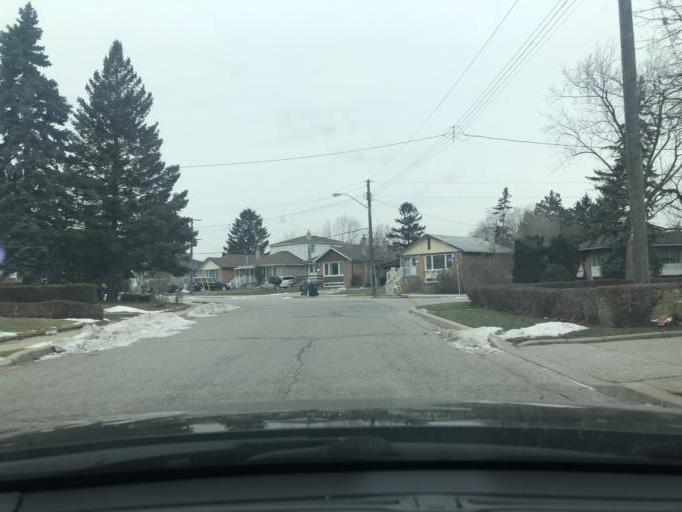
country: CA
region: Ontario
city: Scarborough
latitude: 43.7667
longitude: -79.3043
